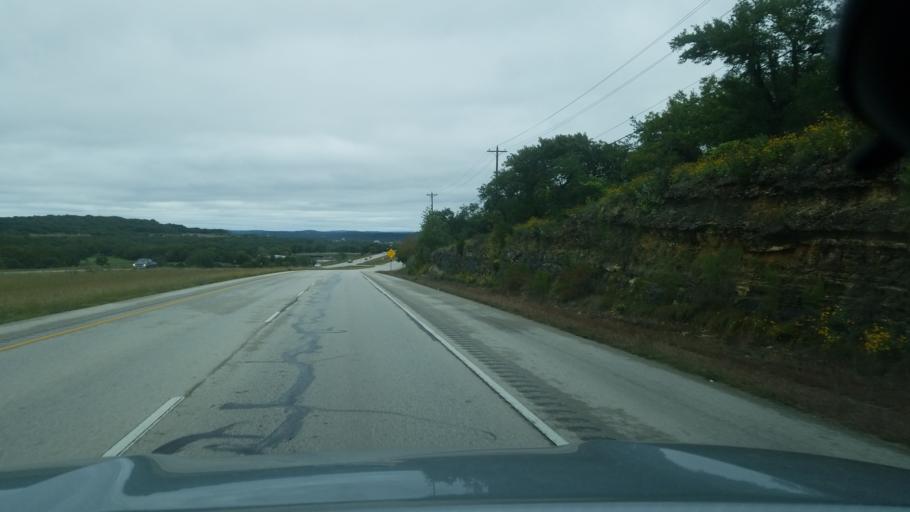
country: US
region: Texas
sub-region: Comal County
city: Bulverde
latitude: 29.8251
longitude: -98.4162
